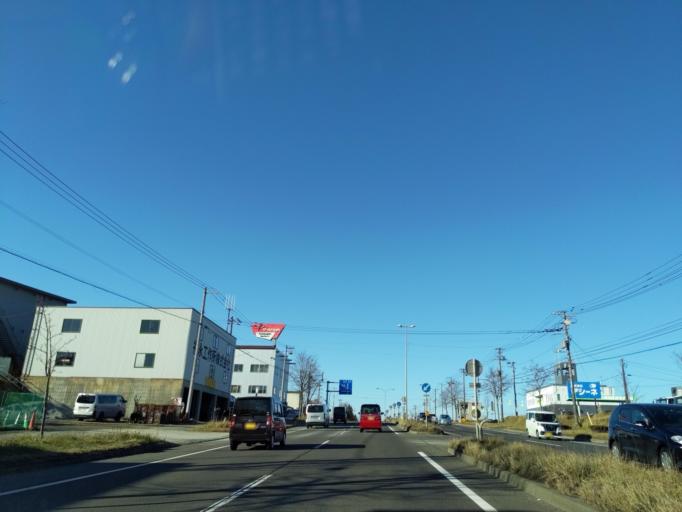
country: JP
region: Hokkaido
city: Kitahiroshima
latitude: 42.9604
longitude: 141.4928
